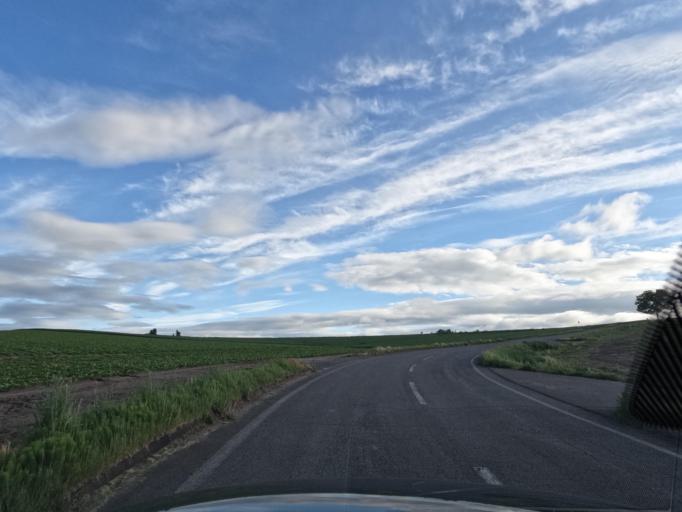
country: JP
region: Hokkaido
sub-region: Asahikawa-shi
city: Asahikawa
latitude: 43.6303
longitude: 142.4333
